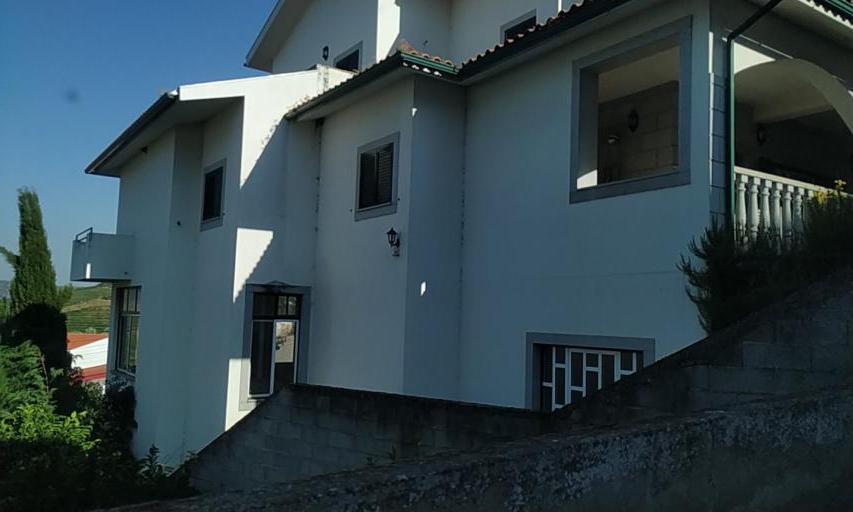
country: PT
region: Viseu
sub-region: Sao Joao da Pesqueira
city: Sao Joao da Pesqueira
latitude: 41.1853
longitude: -7.4146
